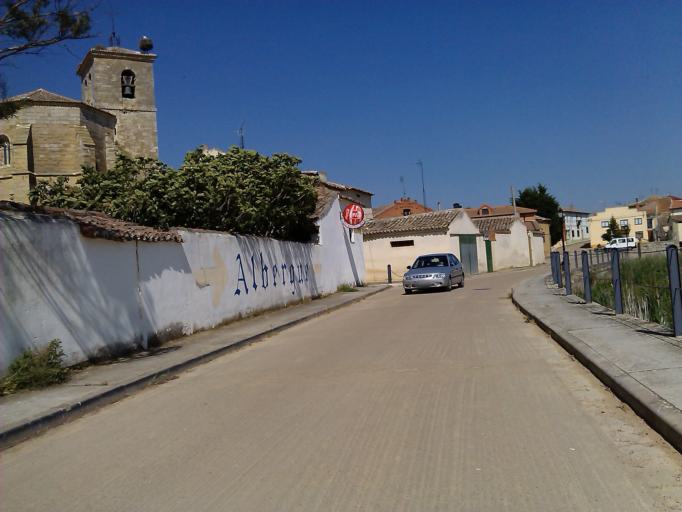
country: ES
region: Castille and Leon
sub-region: Provincia de Palencia
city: Boadilla del Camino
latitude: 42.2585
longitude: -4.3460
